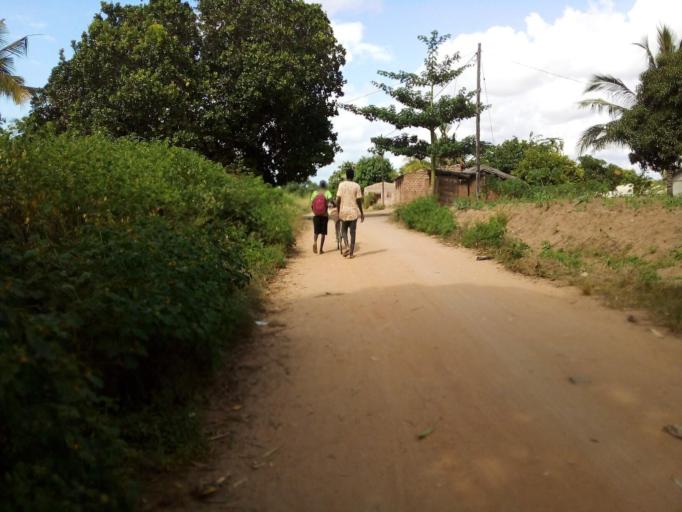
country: MZ
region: Zambezia
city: Quelimane
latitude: -17.5557
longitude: 36.6983
